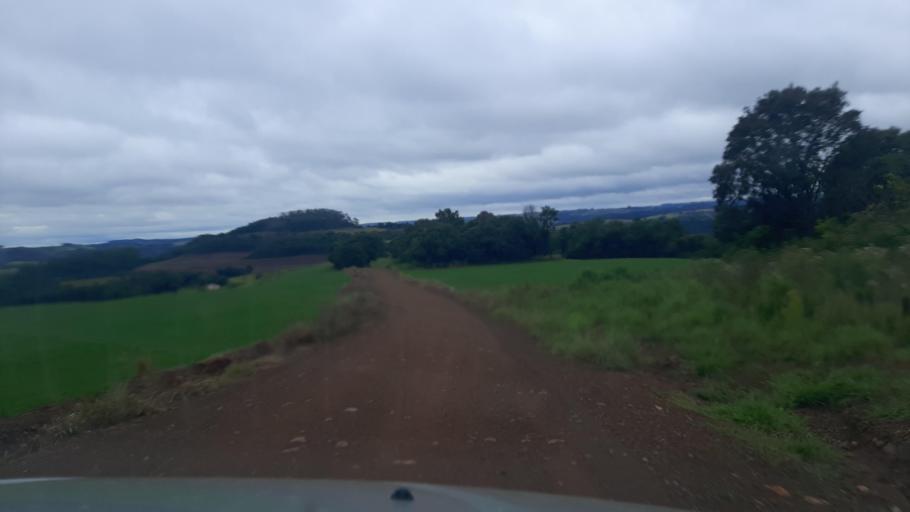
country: BR
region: Parana
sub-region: Ampere
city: Ampere
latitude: -26.0494
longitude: -53.5543
